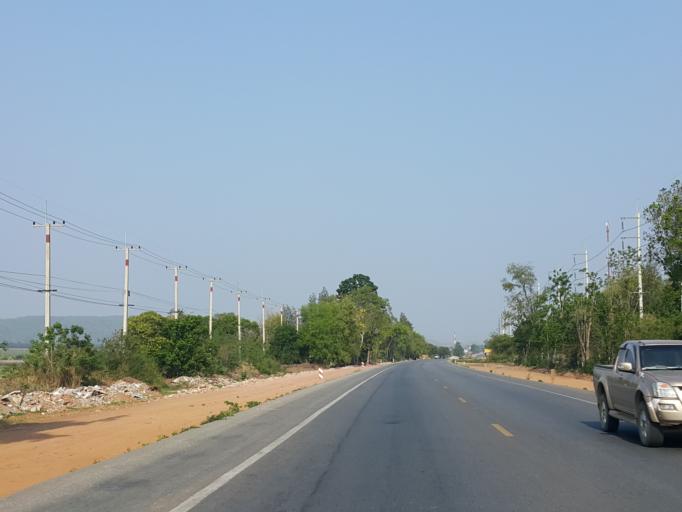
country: TH
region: Kanchanaburi
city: Sai Yok
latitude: 14.0871
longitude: 99.3425
